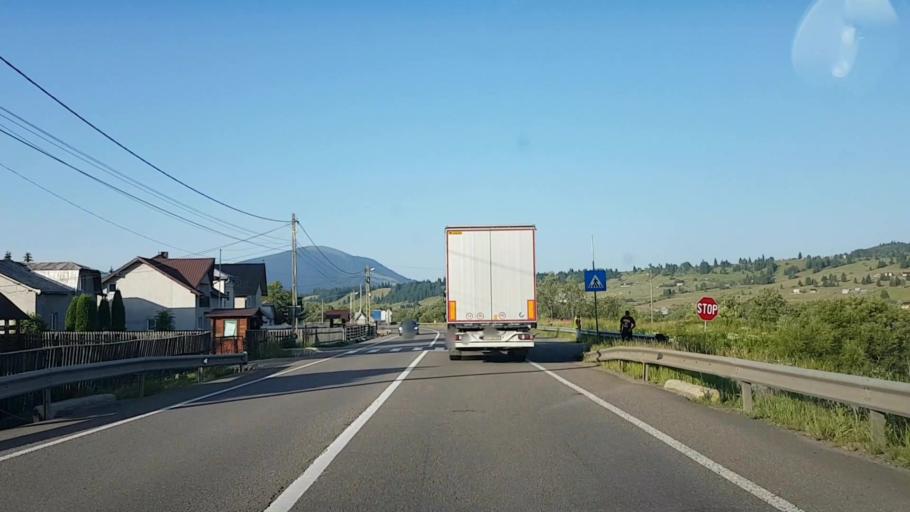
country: RO
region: Suceava
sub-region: Comuna Poiana Stampei
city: Poiana Stampei
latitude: 47.3336
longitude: 25.1597
